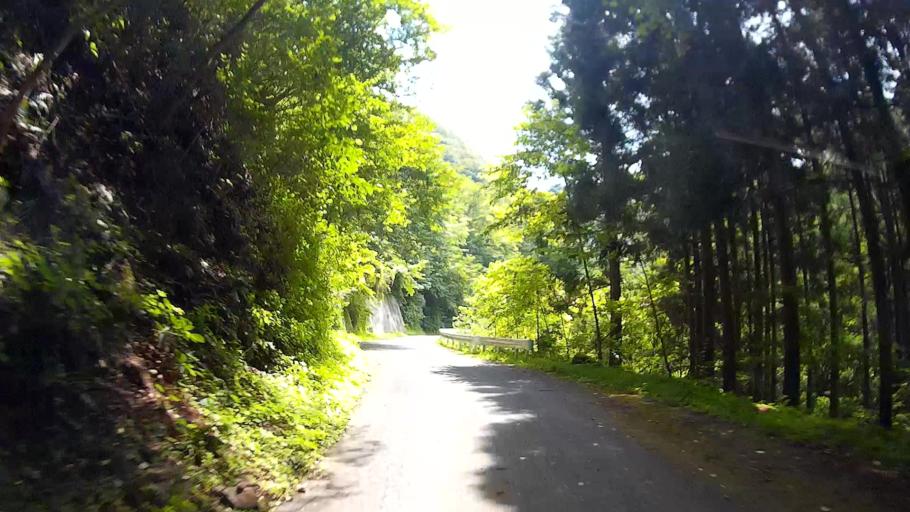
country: JP
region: Saitama
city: Chichibu
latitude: 35.8891
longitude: 139.0990
